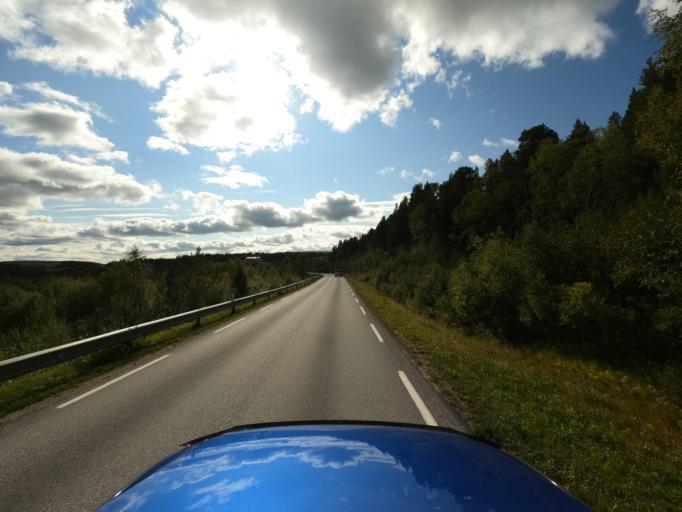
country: NO
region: Finnmark Fylke
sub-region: Karasjok
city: Karasjohka
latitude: 69.4047
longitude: 25.8094
